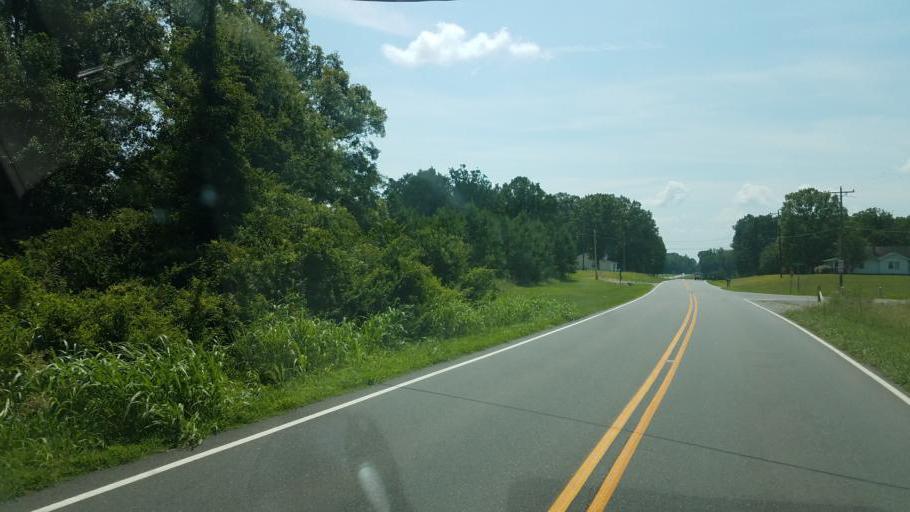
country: US
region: North Carolina
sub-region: Gaston County
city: Cherryville
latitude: 35.3552
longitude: -81.3565
